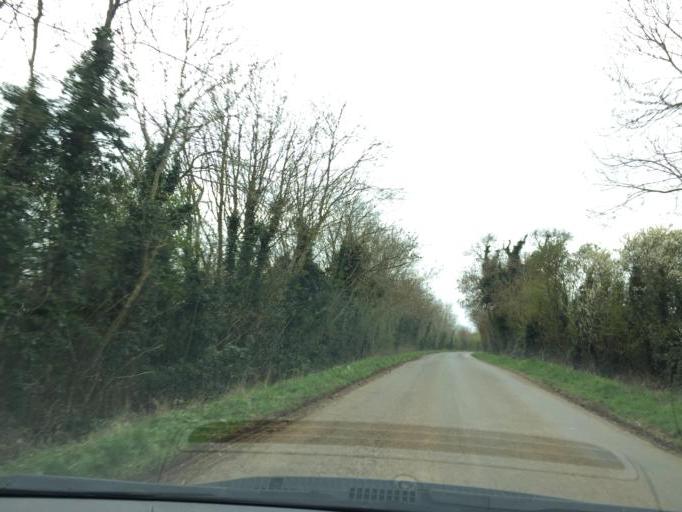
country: GB
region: England
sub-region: Oxfordshire
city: Hanwell
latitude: 52.1030
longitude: -1.4175
